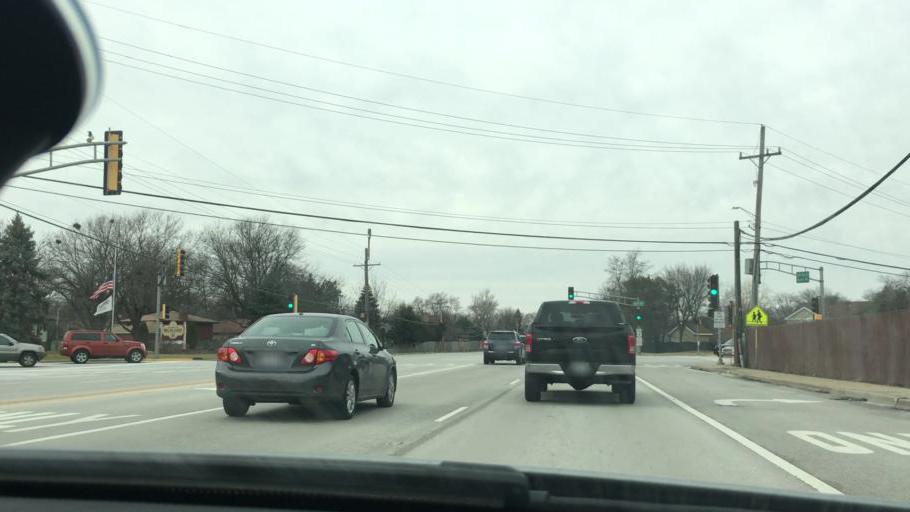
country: US
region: Illinois
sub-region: Cook County
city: Mount Prospect
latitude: 42.0606
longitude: -87.9096
